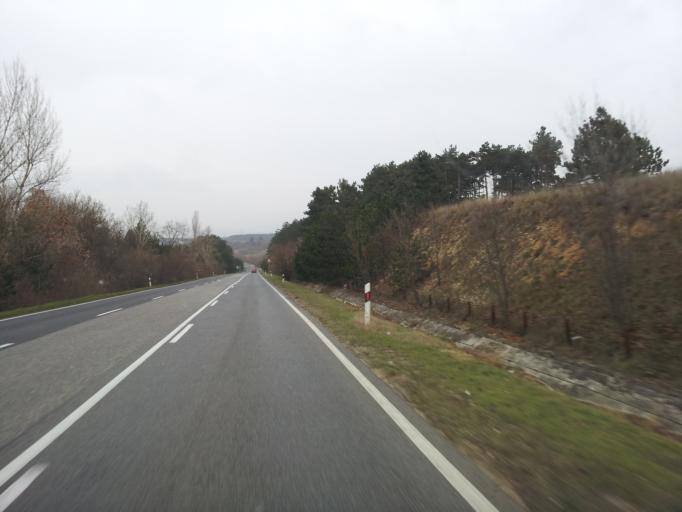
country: HU
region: Veszprem
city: Veszprem
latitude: 47.0917
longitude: 17.8773
